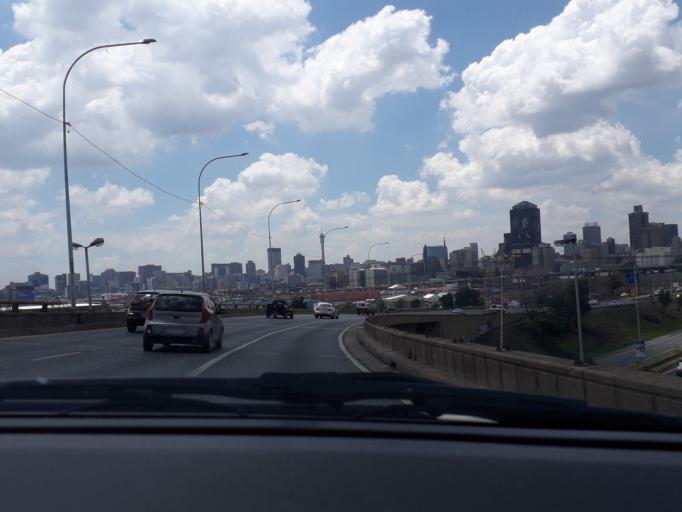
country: ZA
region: Gauteng
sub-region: City of Johannesburg Metropolitan Municipality
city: Johannesburg
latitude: -26.2133
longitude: 28.0239
